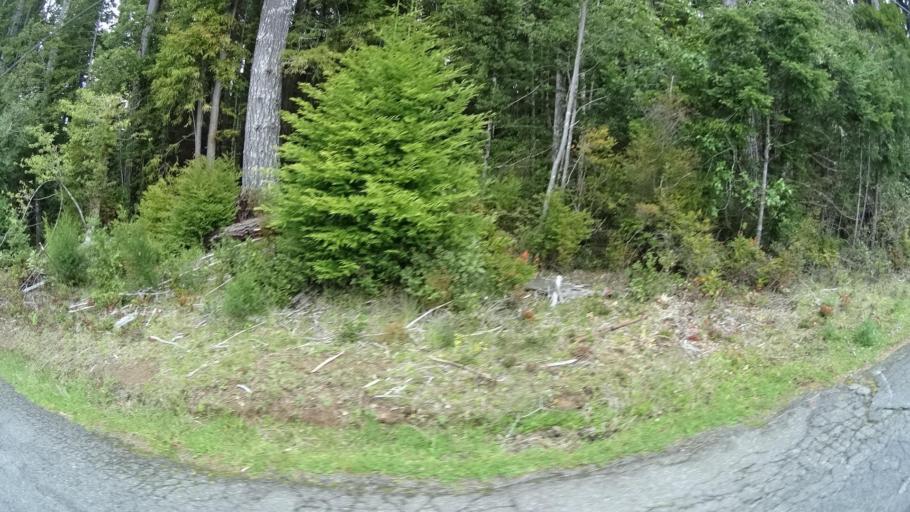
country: US
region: California
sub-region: Humboldt County
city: Blue Lake
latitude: 40.8141
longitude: -123.9929
